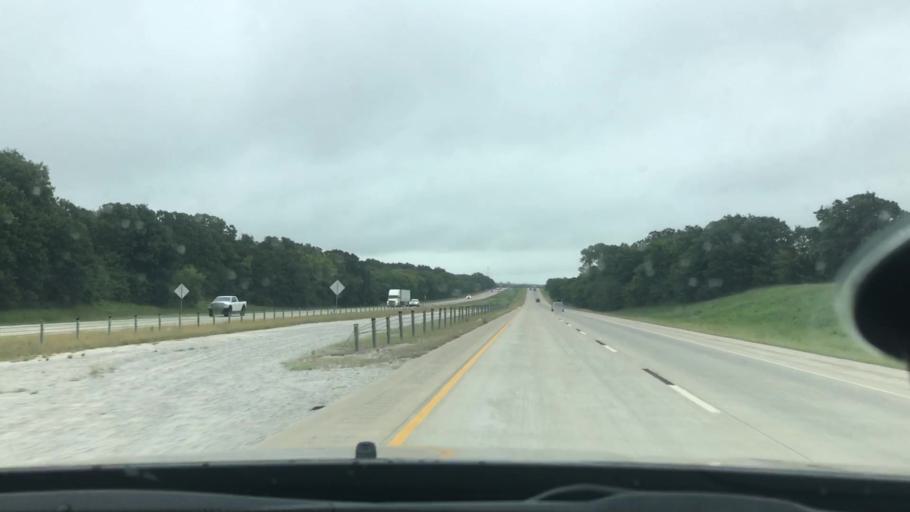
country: US
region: Oklahoma
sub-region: Okmulgee County
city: Wilson
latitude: 35.4275
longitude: -96.0862
